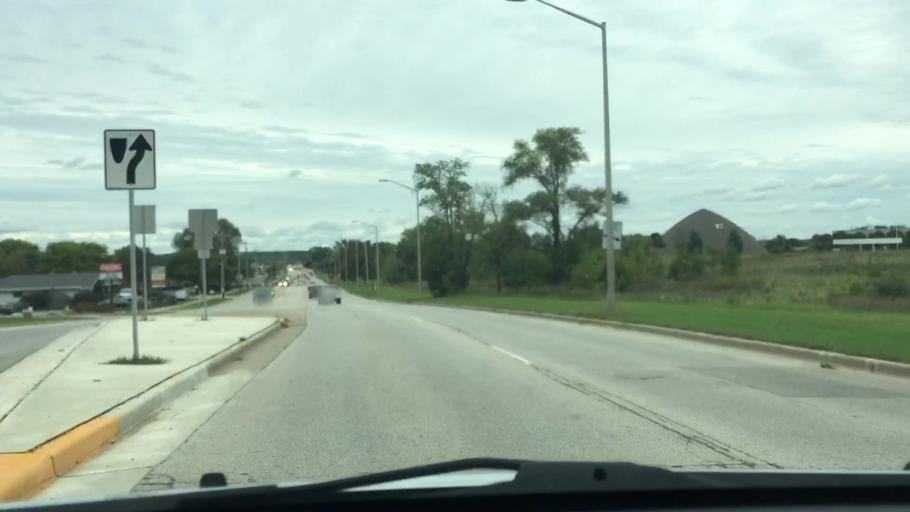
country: US
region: Wisconsin
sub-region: Waukesha County
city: Waukesha
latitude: 43.0333
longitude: -88.2559
